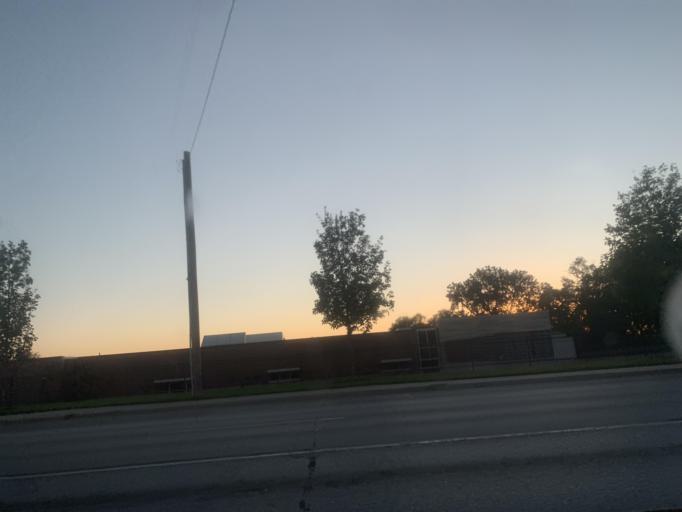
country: US
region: Nebraska
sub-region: Douglas County
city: Omaha
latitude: 41.2131
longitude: -95.9763
